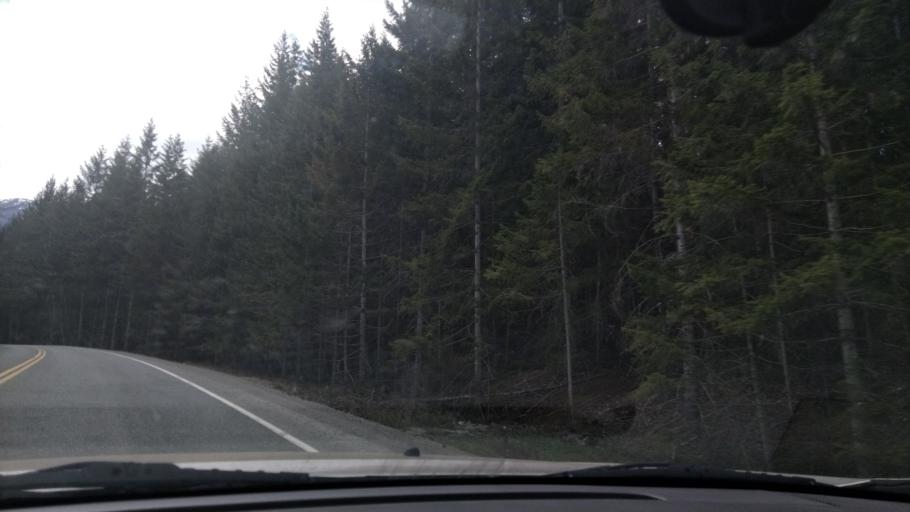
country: CA
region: British Columbia
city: Campbell River
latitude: 49.8733
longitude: -125.6577
